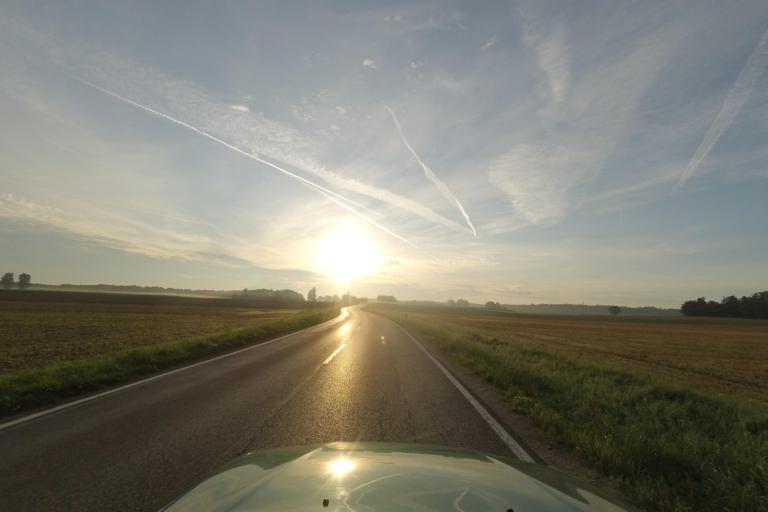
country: DE
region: Bavaria
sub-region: Upper Bavaria
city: Moorenweis
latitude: 48.1534
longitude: 11.0922
